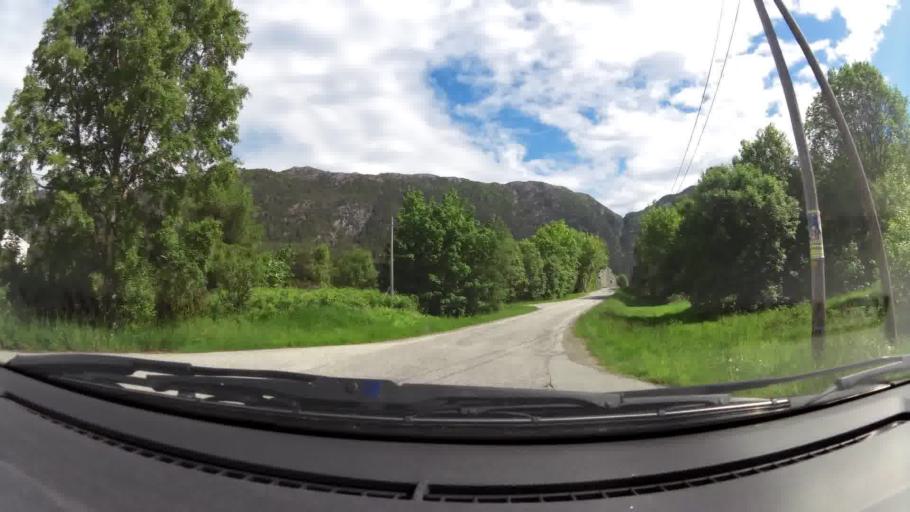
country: NO
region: More og Romsdal
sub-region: Kristiansund
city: Kristiansund
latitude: 63.0600
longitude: 7.7086
